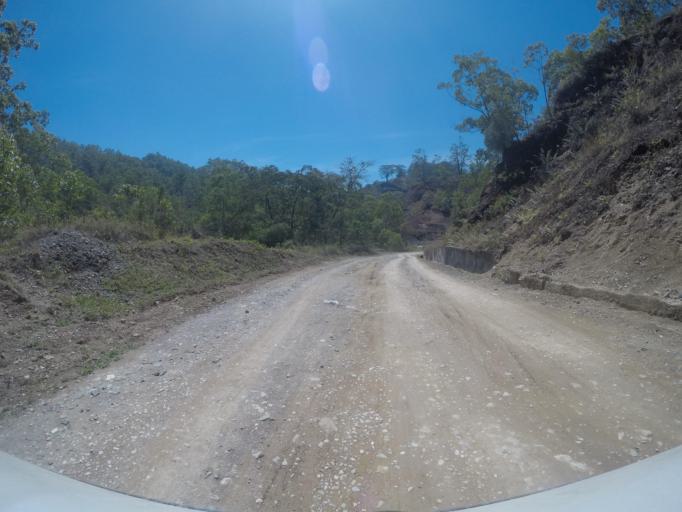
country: TL
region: Ermera
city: Gleno
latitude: -8.7795
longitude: 125.3806
